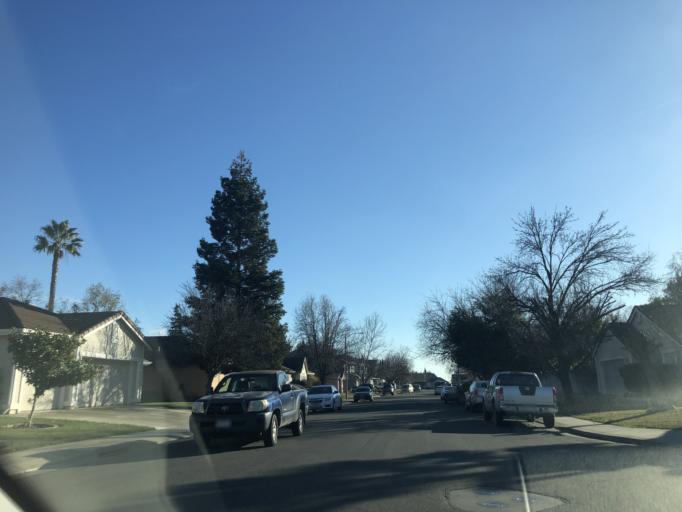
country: US
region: California
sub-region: Yolo County
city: Woodland
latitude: 38.6655
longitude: -121.7444
